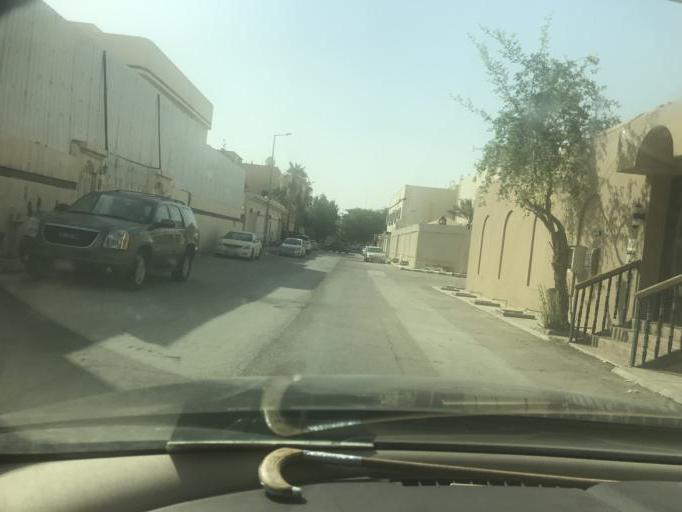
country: SA
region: Ar Riyad
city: Riyadh
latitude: 24.7382
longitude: 46.7783
